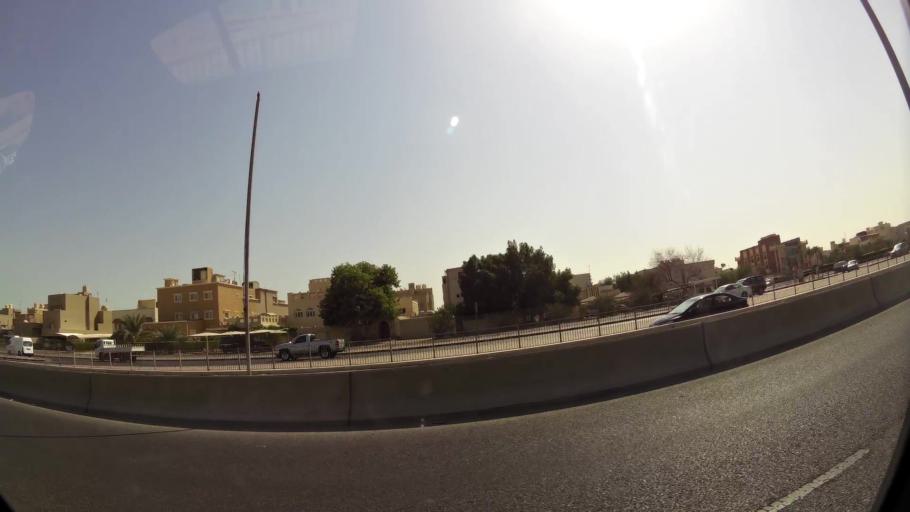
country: KW
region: Muhafazat Hawalli
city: As Salimiyah
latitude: 29.3256
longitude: 48.0724
